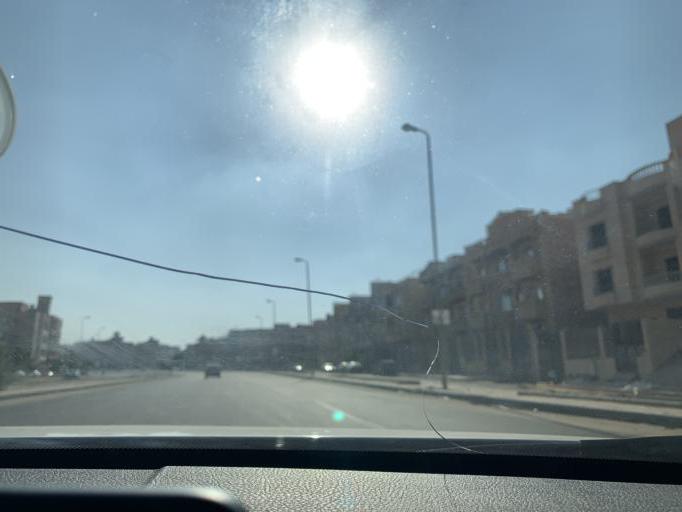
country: EG
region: Muhafazat al Qalyubiyah
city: Al Khankah
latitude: 30.0050
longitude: 31.4812
